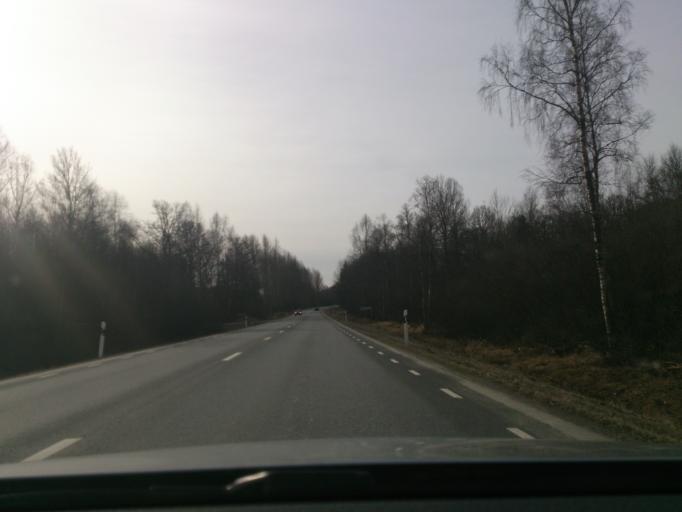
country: SE
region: Kronoberg
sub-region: Alvesta Kommun
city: Alvesta
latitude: 56.9307
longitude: 14.5593
